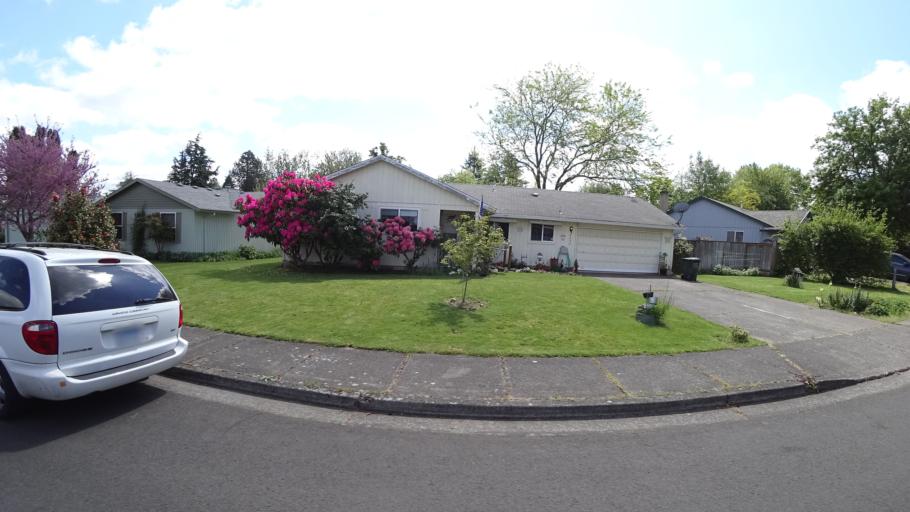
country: US
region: Oregon
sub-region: Washington County
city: Aloha
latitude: 45.5052
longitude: -122.8886
